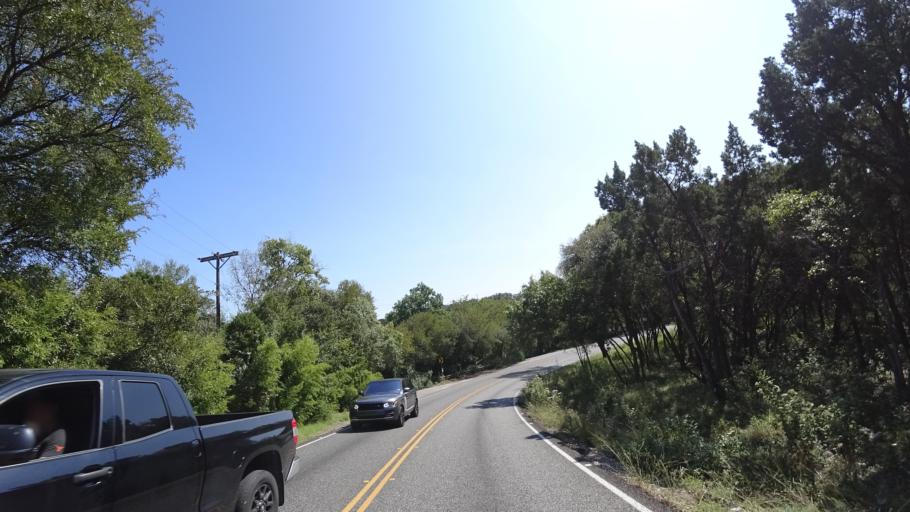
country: US
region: Texas
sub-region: Travis County
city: West Lake Hills
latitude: 30.2993
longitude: -97.7937
